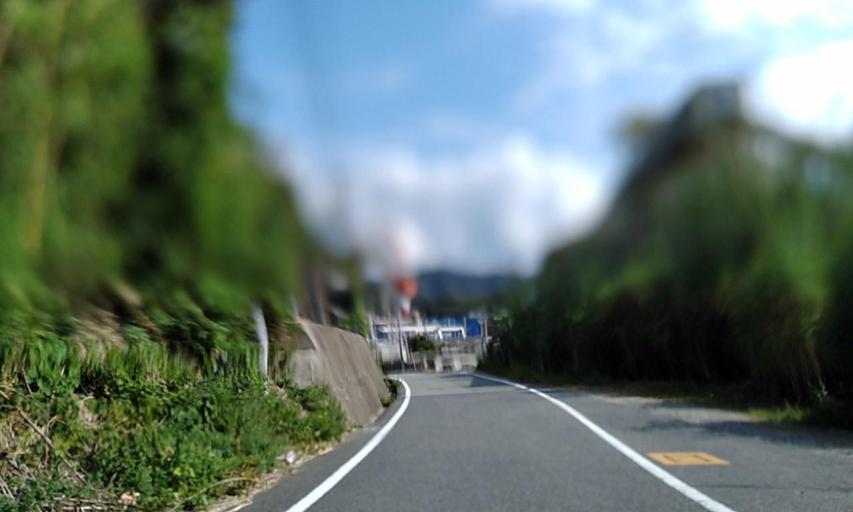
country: JP
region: Wakayama
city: Gobo
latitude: 33.9646
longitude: 135.1071
